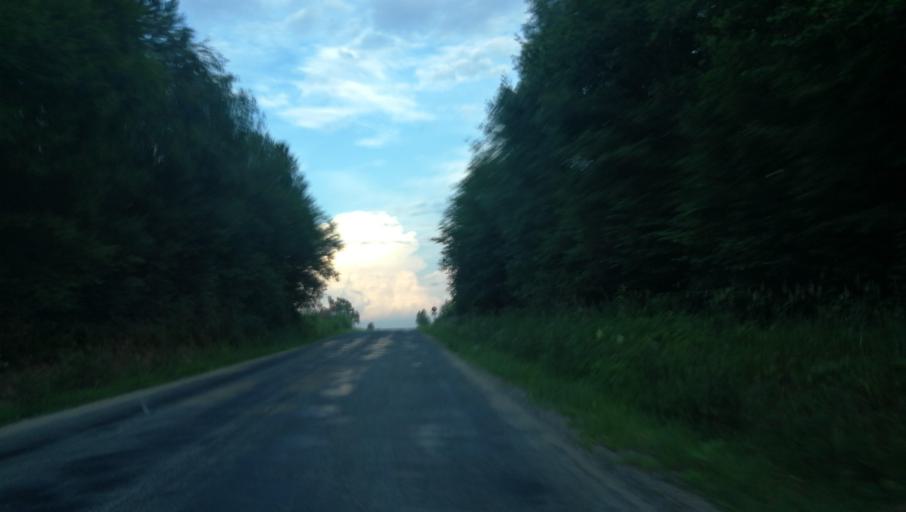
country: LV
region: Priekuli
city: Priekuli
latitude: 57.2718
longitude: 25.3370
